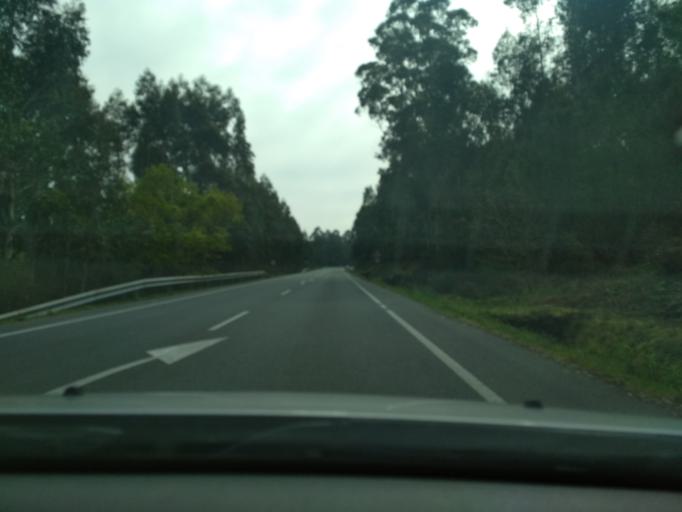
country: ES
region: Galicia
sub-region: Provincia de Pontevedra
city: Catoira
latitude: 42.6530
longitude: -8.7002
